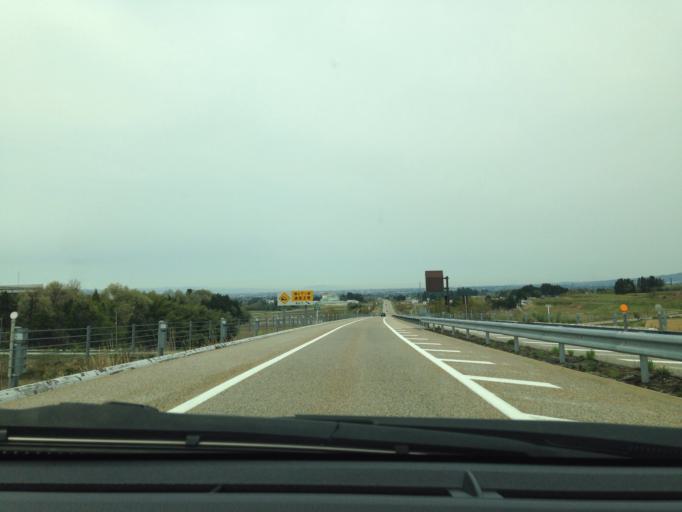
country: JP
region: Toyama
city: Fukumitsu
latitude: 36.5083
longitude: 136.8759
